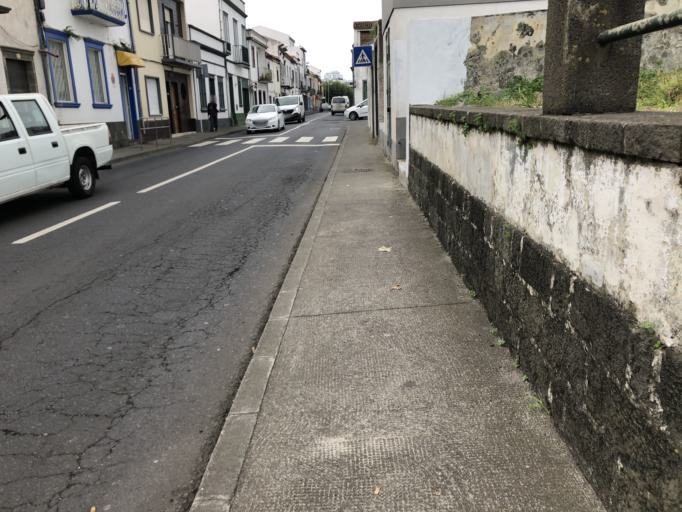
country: PT
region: Azores
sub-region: Ponta Delgada
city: Rosto de Cao
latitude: 37.7429
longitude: -25.6527
